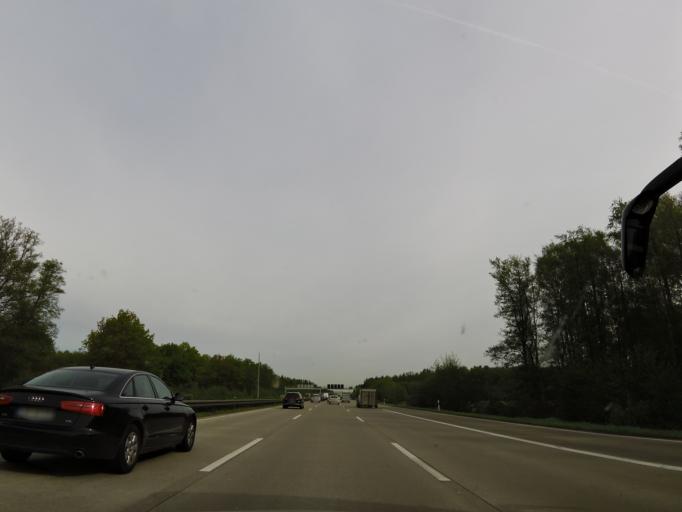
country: DE
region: Lower Saxony
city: Isernhagen Farster Bauerschaft
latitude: 52.5079
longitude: 9.8228
